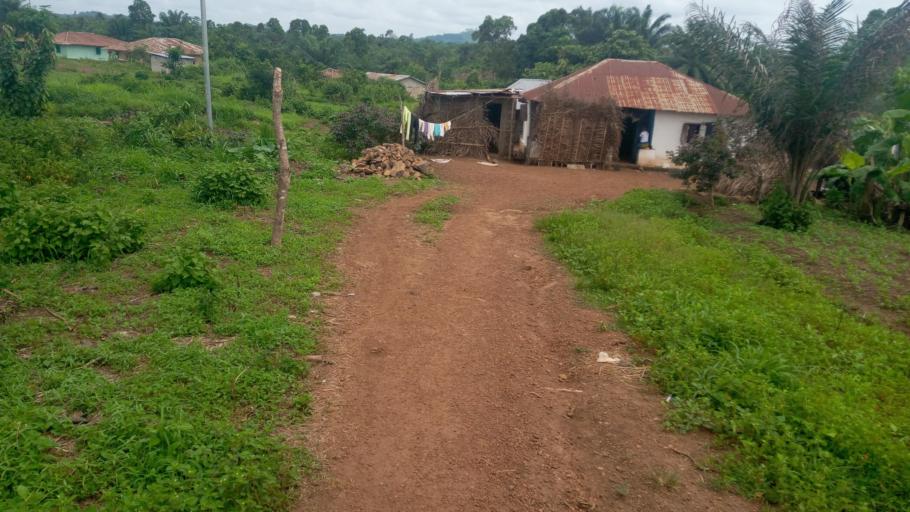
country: SL
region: Southern Province
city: Mogbwemo
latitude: 7.7773
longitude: -12.3026
